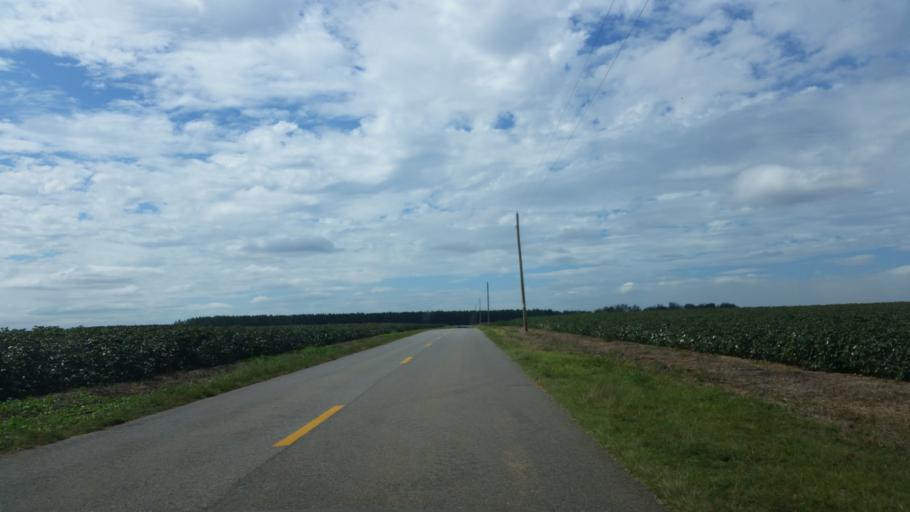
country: US
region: Florida
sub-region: Santa Rosa County
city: Point Baker
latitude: 30.7365
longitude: -87.0221
